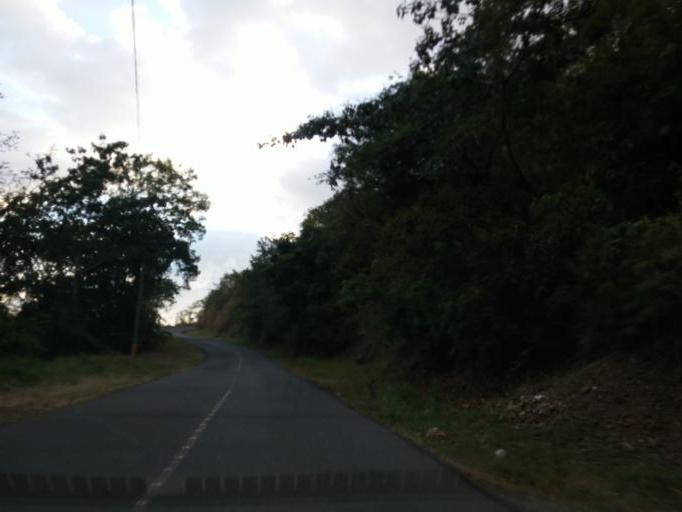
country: CR
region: San Jose
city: Palmichal
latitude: 9.8301
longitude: -84.2004
